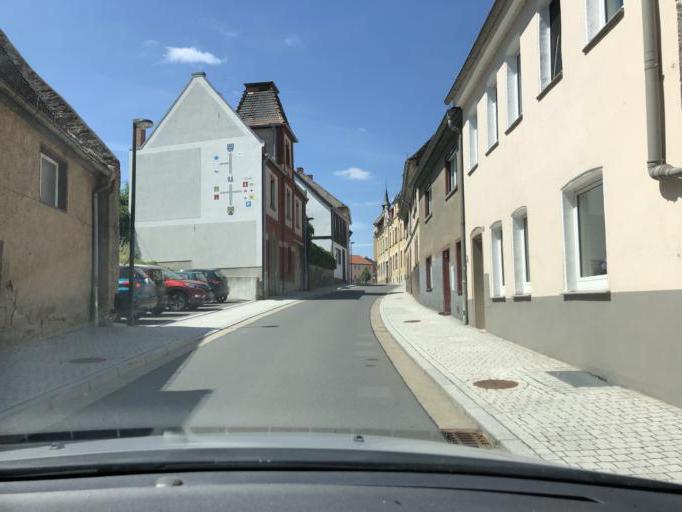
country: DE
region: Saxony-Anhalt
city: Osterfeld
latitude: 51.0802
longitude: 11.9320
